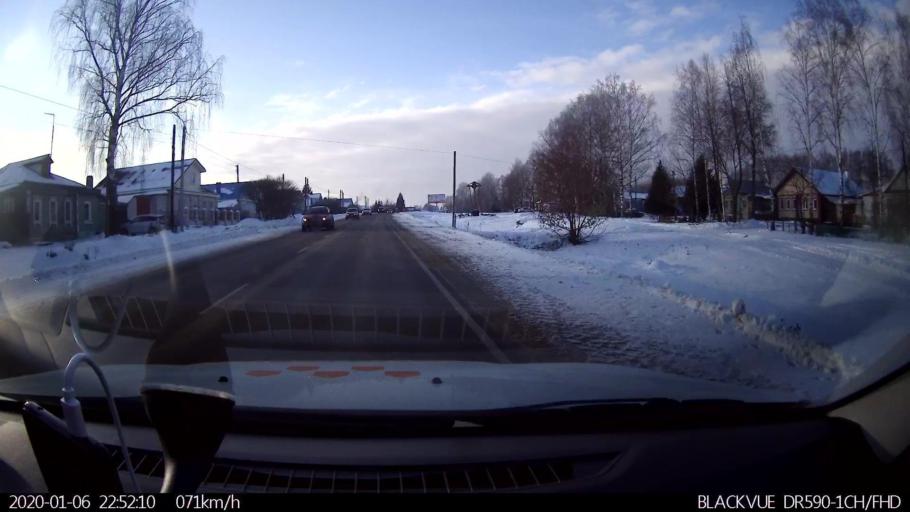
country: RU
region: Nizjnij Novgorod
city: Bogorodsk
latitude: 56.1279
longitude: 43.5869
